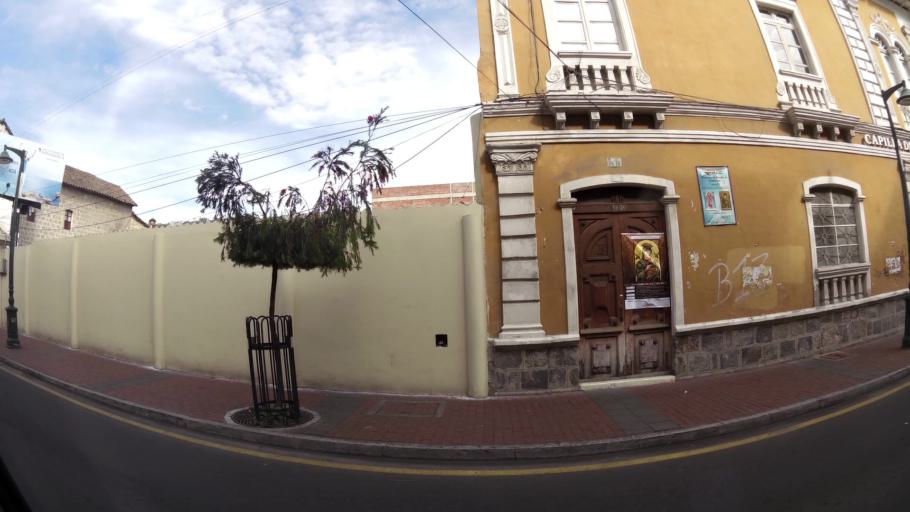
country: EC
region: Tungurahua
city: Ambato
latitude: -1.2406
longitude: -78.6280
